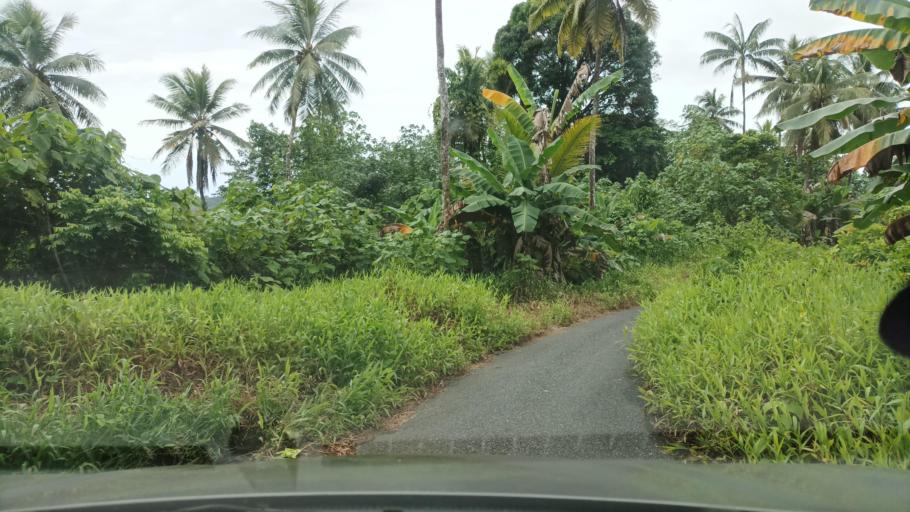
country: FM
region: Pohnpei
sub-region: Madolenihm Municipality
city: Madolenihm Municipality Government
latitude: 6.9140
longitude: 158.2883
